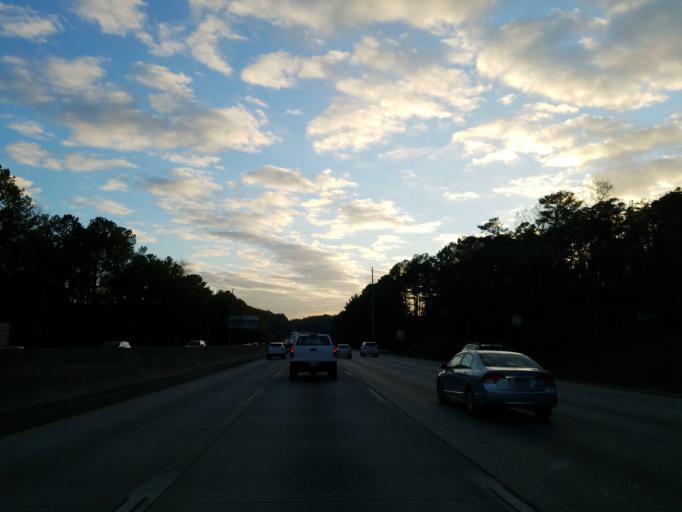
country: US
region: Georgia
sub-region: Fulton County
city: Roswell
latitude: 34.0146
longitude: -84.3295
